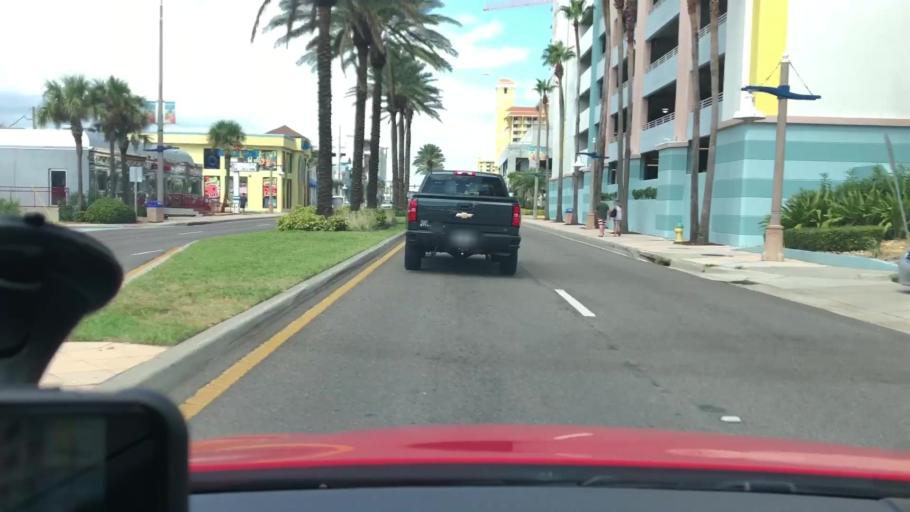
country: US
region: Florida
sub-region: Volusia County
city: Daytona Beach
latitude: 29.2320
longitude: -81.0107
